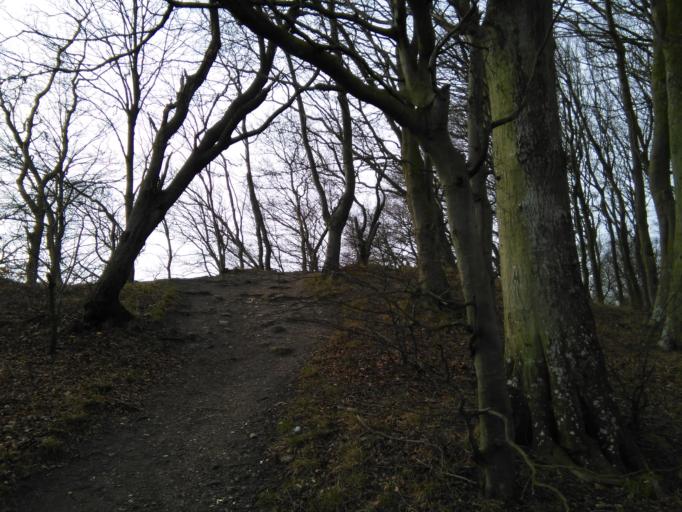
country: DK
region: Central Jutland
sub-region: Arhus Kommune
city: Beder
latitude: 56.0912
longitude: 10.2481
